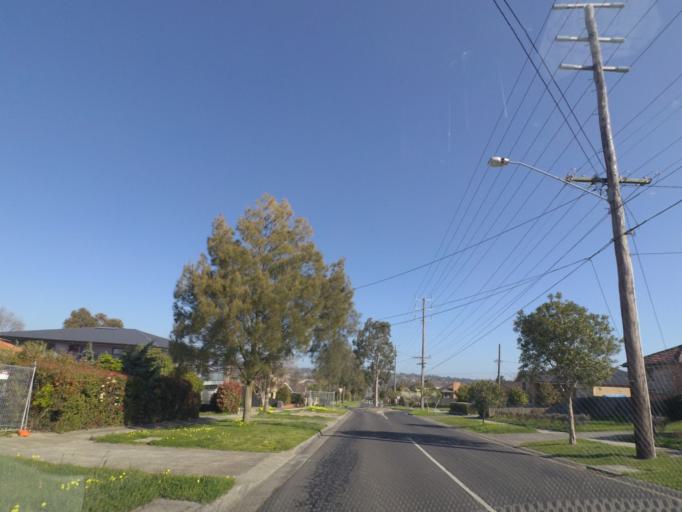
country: AU
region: Victoria
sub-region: Manningham
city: Templestowe Lower
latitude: -37.7737
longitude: 145.1045
